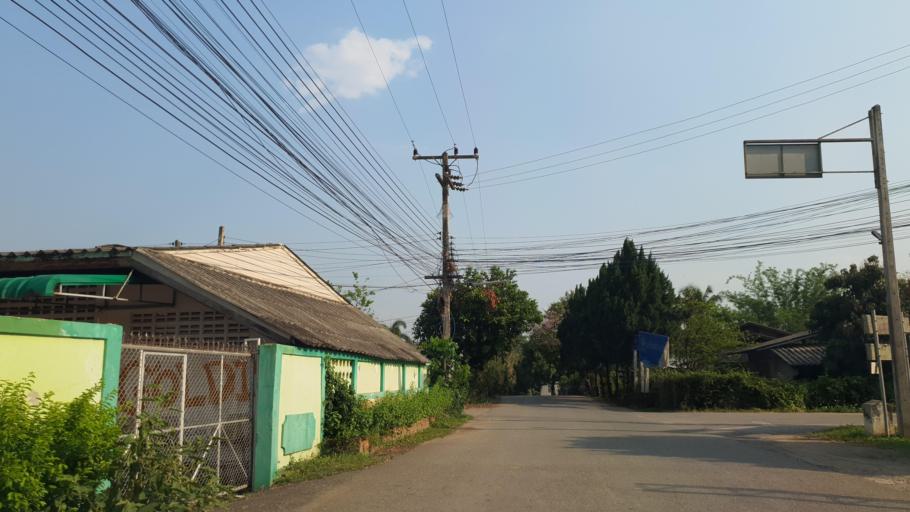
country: TH
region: Chiang Mai
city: Mae Wang
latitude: 18.6721
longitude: 98.8141
